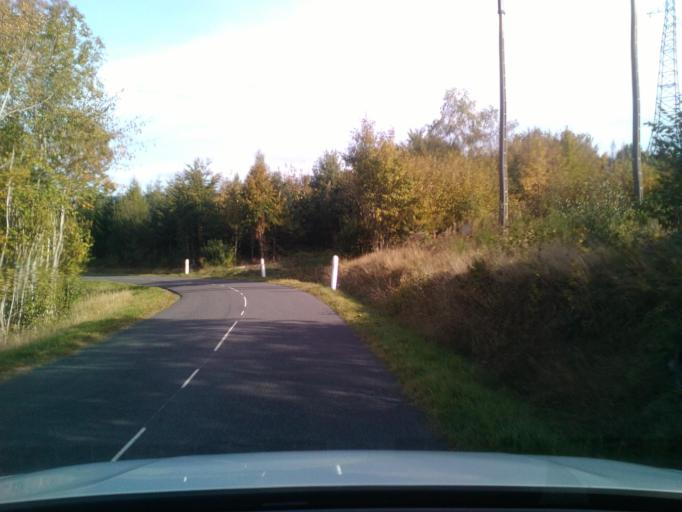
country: FR
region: Lorraine
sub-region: Departement des Vosges
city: Senones
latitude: 48.3742
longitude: 7.0406
